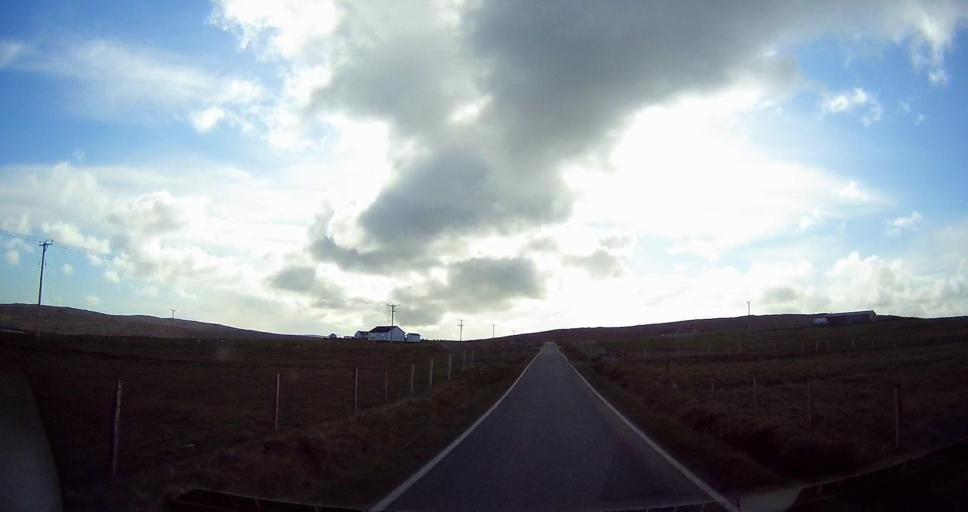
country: GB
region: Scotland
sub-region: Shetland Islands
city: Shetland
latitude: 60.3562
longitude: -1.1559
